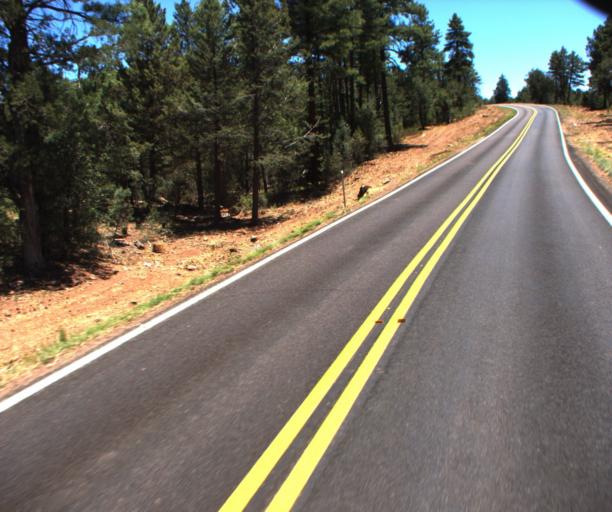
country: US
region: Arizona
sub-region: Gila County
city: Pine
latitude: 34.3659
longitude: -111.4333
